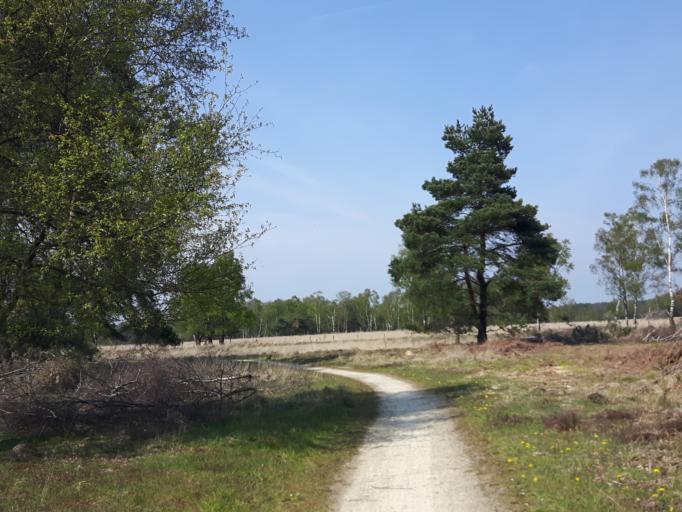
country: NL
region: Overijssel
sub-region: Gemeente Haaksbergen
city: Haaksbergen
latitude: 52.1327
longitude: 6.7846
